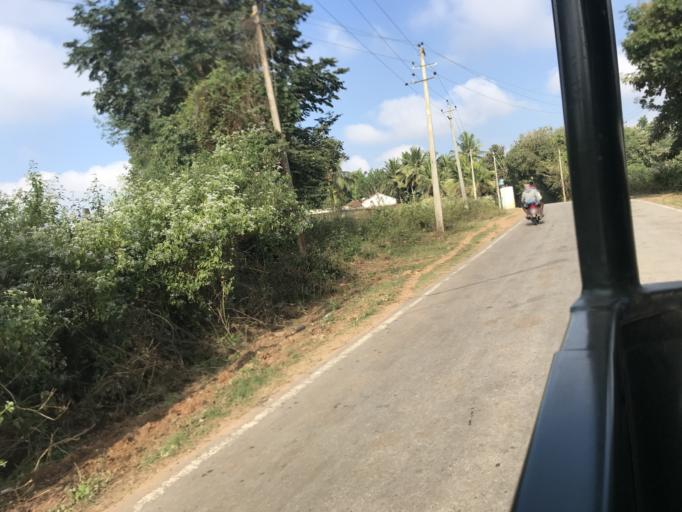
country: IN
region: Karnataka
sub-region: Mysore
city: Heggadadevankote
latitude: 11.9445
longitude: 76.2438
